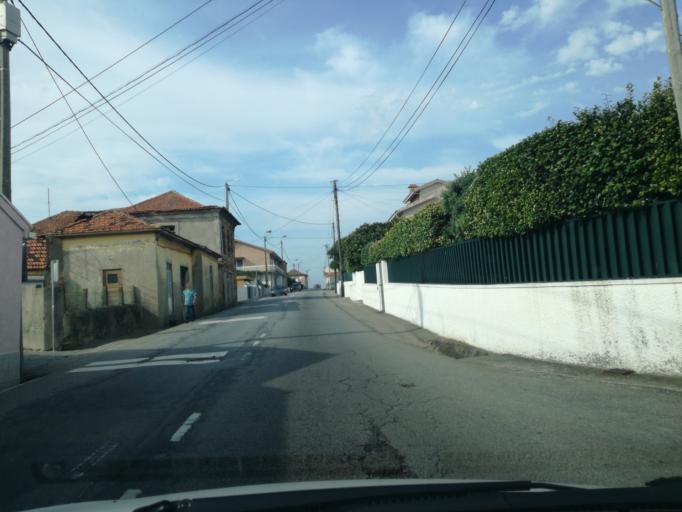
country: PT
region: Aveiro
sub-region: Espinho
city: Espinho
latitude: 41.0182
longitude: -8.6319
